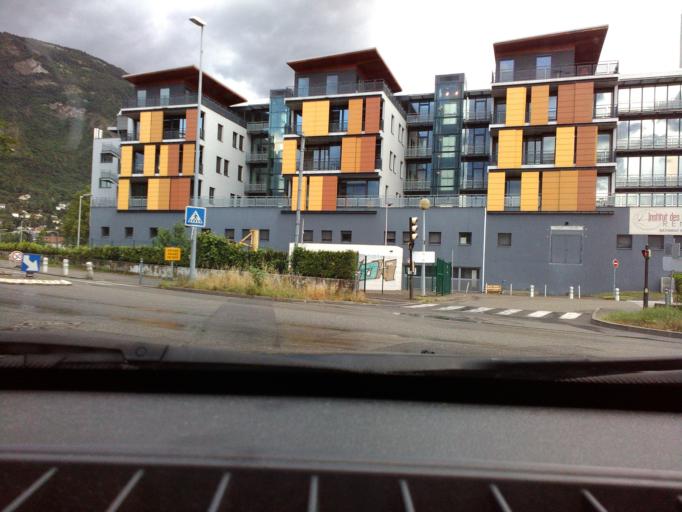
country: FR
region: Rhone-Alpes
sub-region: Departement de l'Isere
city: La Tronche
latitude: 45.1980
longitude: 5.7441
